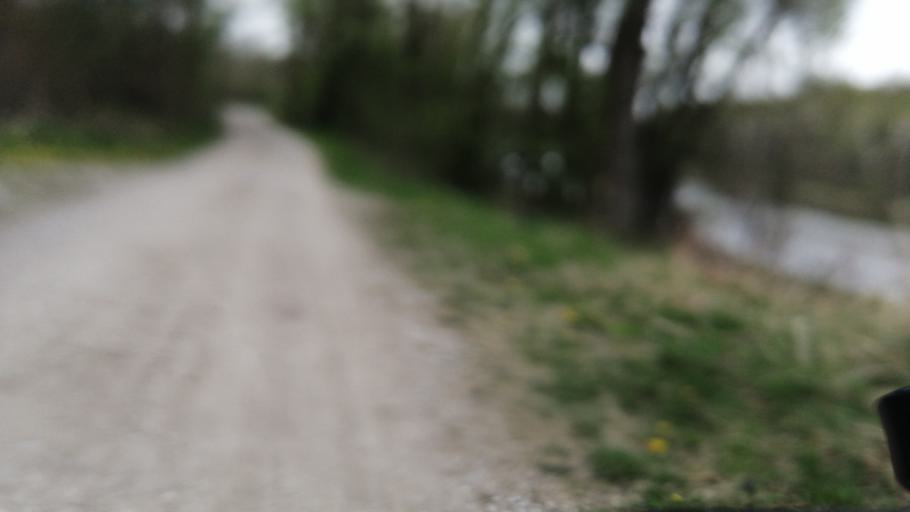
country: DE
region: Bavaria
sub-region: Upper Bavaria
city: Unterfoehring
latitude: 48.2017
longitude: 11.6386
